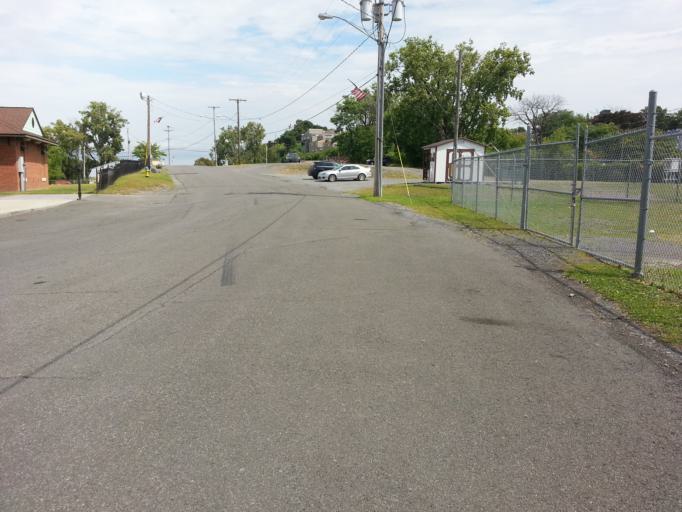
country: US
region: New York
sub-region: Columbia County
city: Hudson
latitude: 42.2538
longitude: -73.7991
